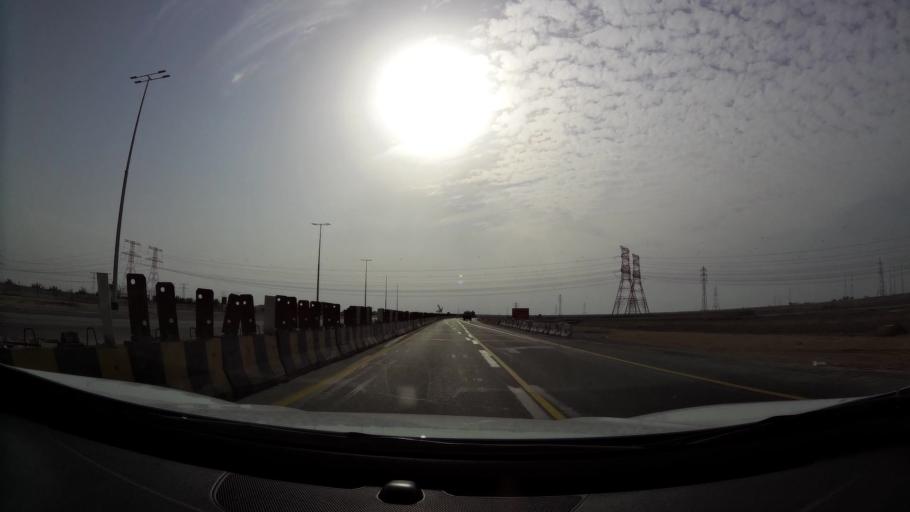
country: AE
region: Abu Dhabi
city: Abu Dhabi
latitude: 24.2217
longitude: 54.4334
